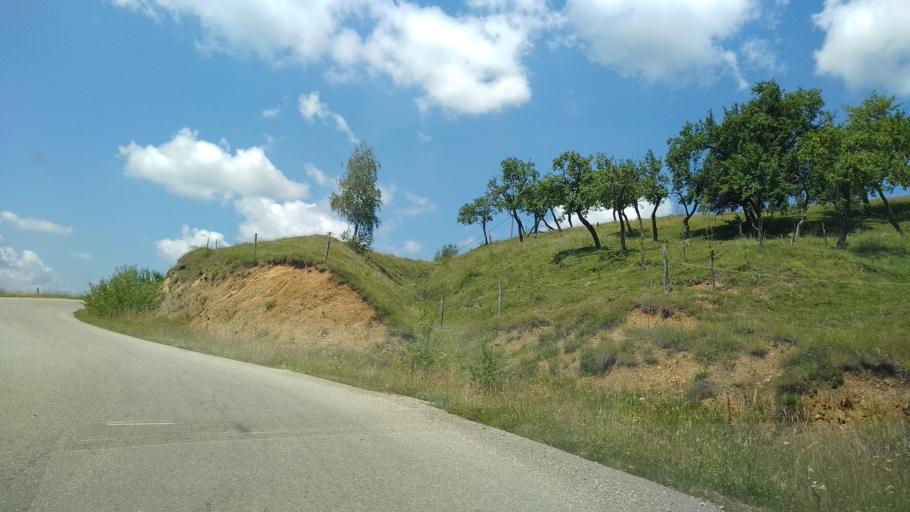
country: RO
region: Hunedoara
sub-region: Comuna Orastioara de Sus
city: Orastioara de Sus
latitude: 45.7067
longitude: 23.1417
